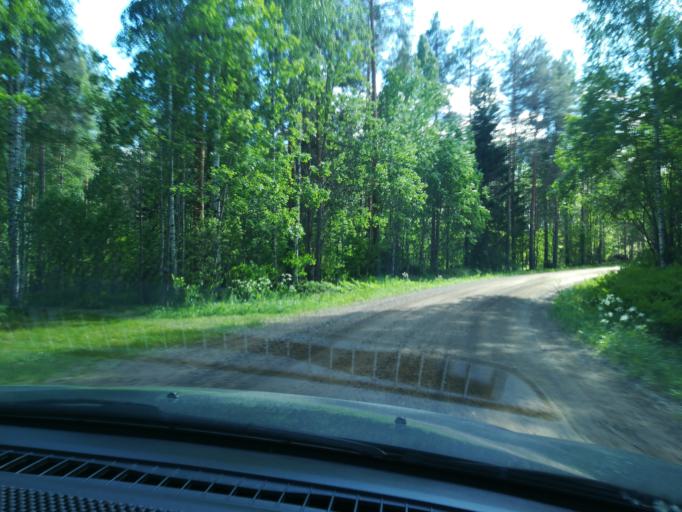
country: FI
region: Southern Savonia
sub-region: Mikkeli
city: Puumala
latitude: 61.6626
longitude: 28.1418
